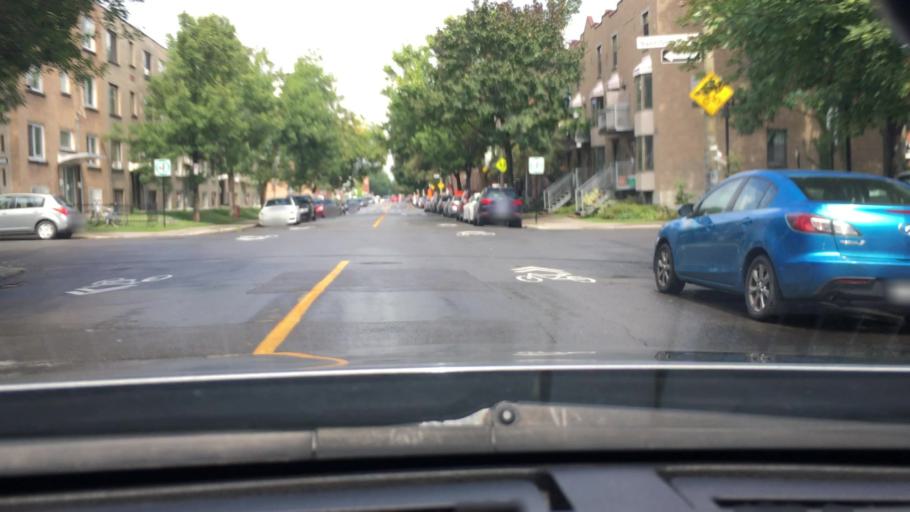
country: CA
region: Quebec
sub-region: Monteregie
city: Longueuil
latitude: 45.5425
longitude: -73.5505
